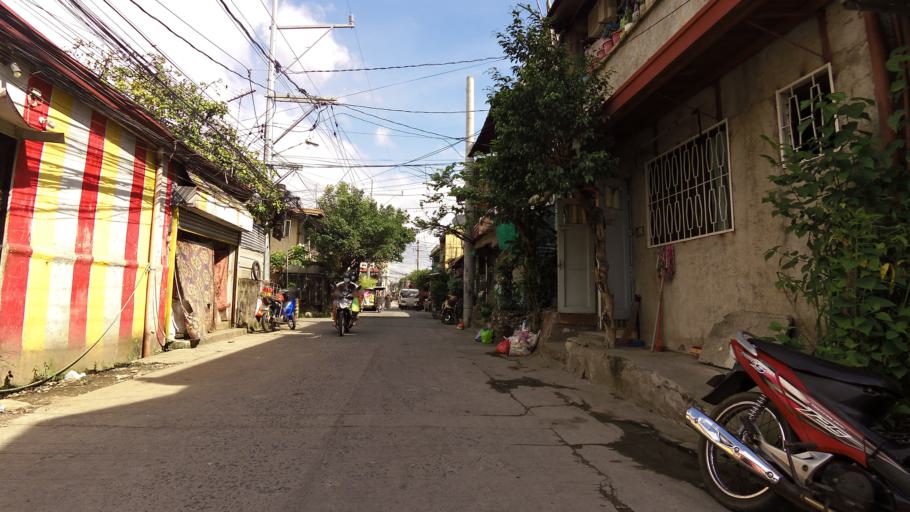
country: PH
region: Calabarzon
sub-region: Province of Rizal
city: Cainta
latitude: 14.5697
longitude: 121.1281
